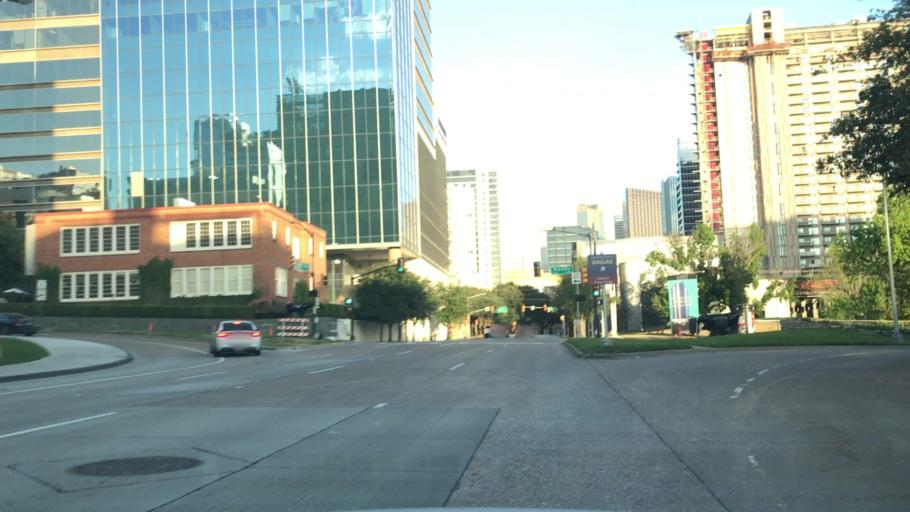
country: US
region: Texas
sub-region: Dallas County
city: Dallas
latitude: 32.7921
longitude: -96.8075
